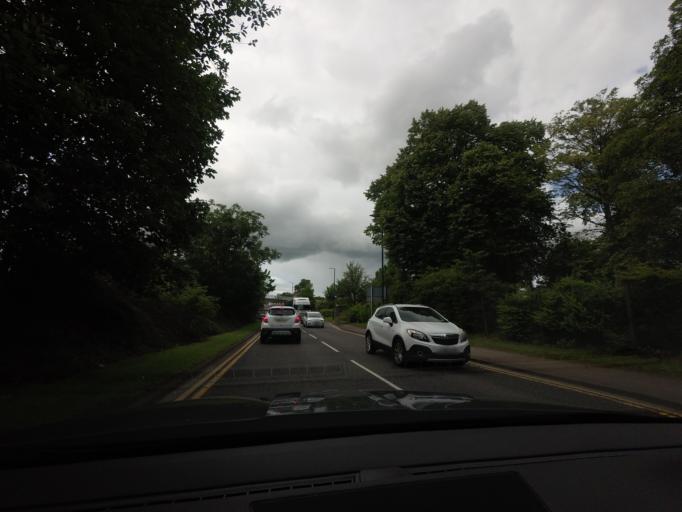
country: GB
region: Scotland
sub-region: Moray
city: Elgin
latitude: 57.6499
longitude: -3.3106
